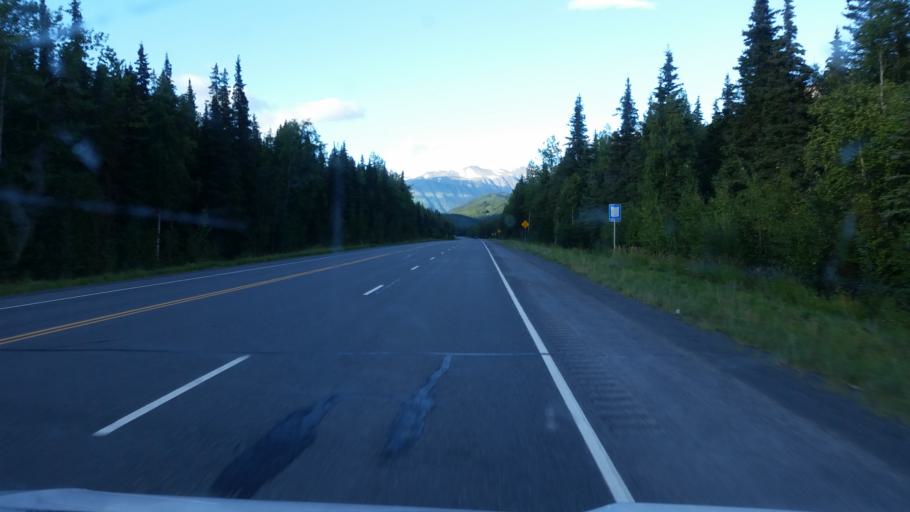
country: US
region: Alaska
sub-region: Kenai Peninsula Borough
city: Bear Creek
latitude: 60.4884
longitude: -149.7206
